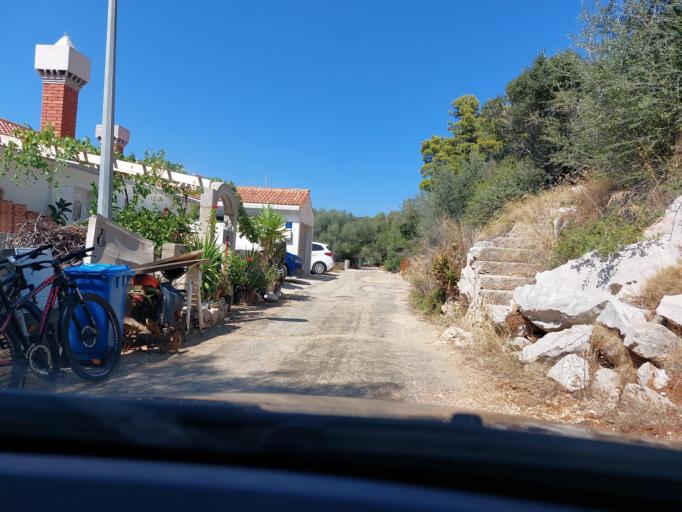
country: HR
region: Dubrovacko-Neretvanska
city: Smokvica
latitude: 42.7726
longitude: 16.8389
